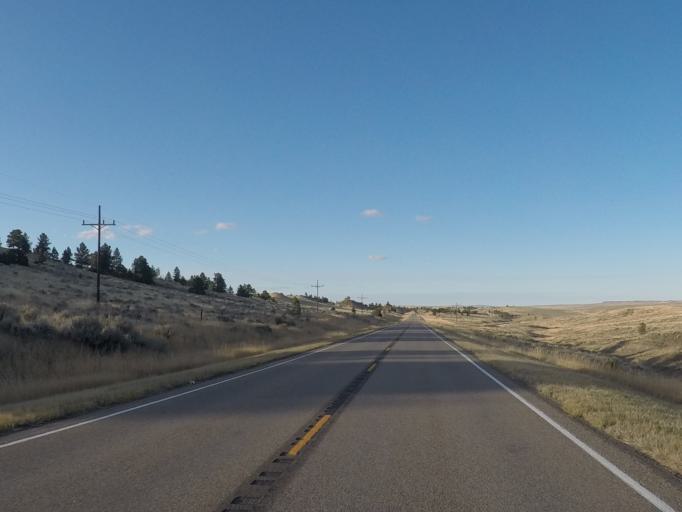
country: US
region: Montana
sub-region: Golden Valley County
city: Ryegate
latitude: 46.2506
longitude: -108.9367
